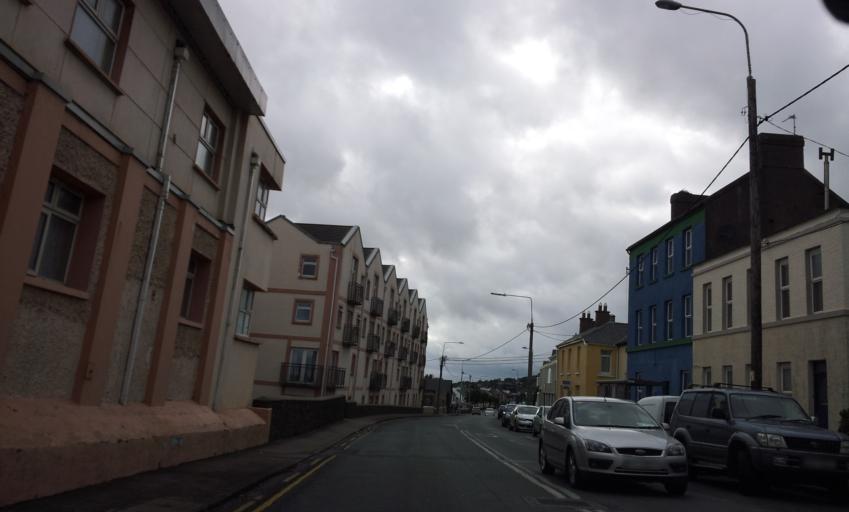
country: IE
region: Munster
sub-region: County Cork
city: Youghal
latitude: 51.9407
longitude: -7.8437
